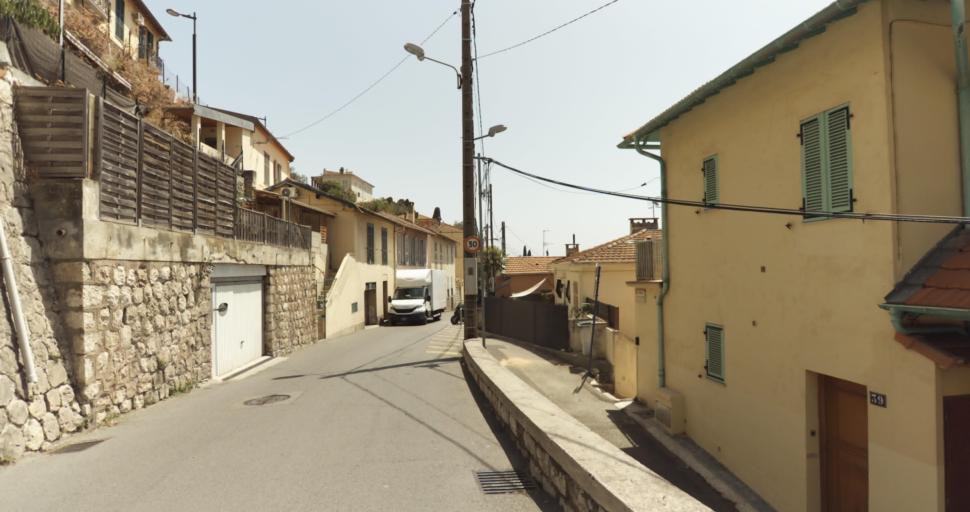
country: FR
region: Provence-Alpes-Cote d'Azur
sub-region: Departement des Alpes-Maritimes
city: Menton
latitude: 43.7804
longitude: 7.5047
